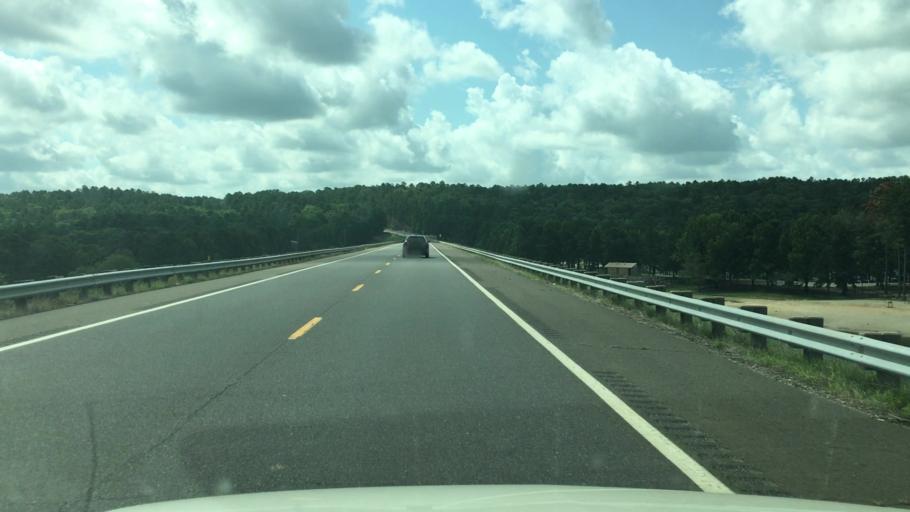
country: US
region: Arkansas
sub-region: Clark County
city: Arkadelphia
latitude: 34.2386
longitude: -93.1030
